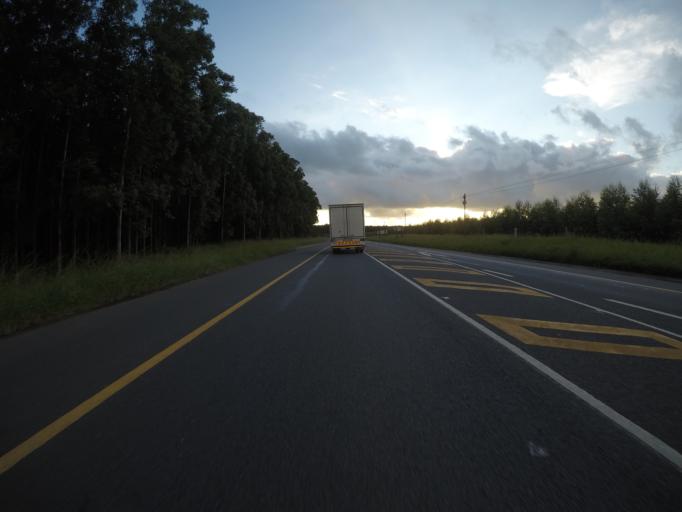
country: ZA
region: KwaZulu-Natal
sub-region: uThungulu District Municipality
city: KwaMbonambi
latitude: -28.5783
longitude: 32.1024
